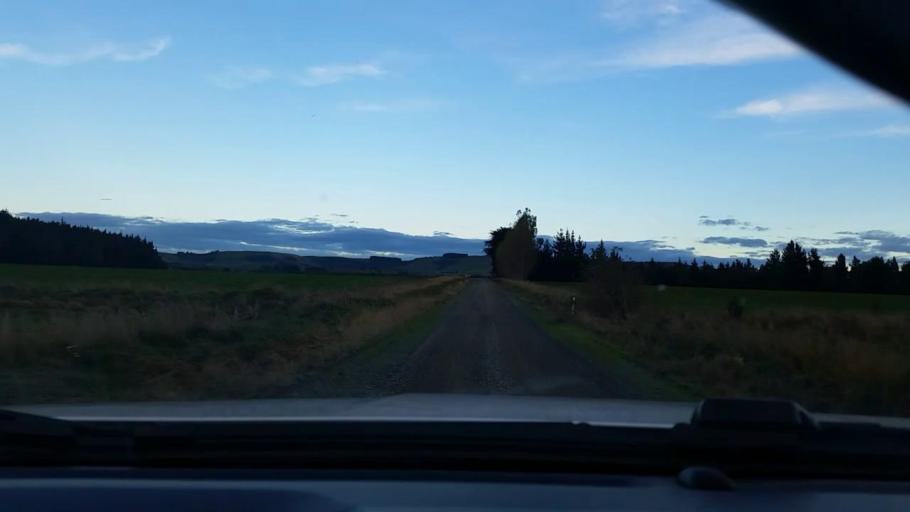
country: NZ
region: Southland
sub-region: Southland District
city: Winton
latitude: -46.1049
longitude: 168.4559
